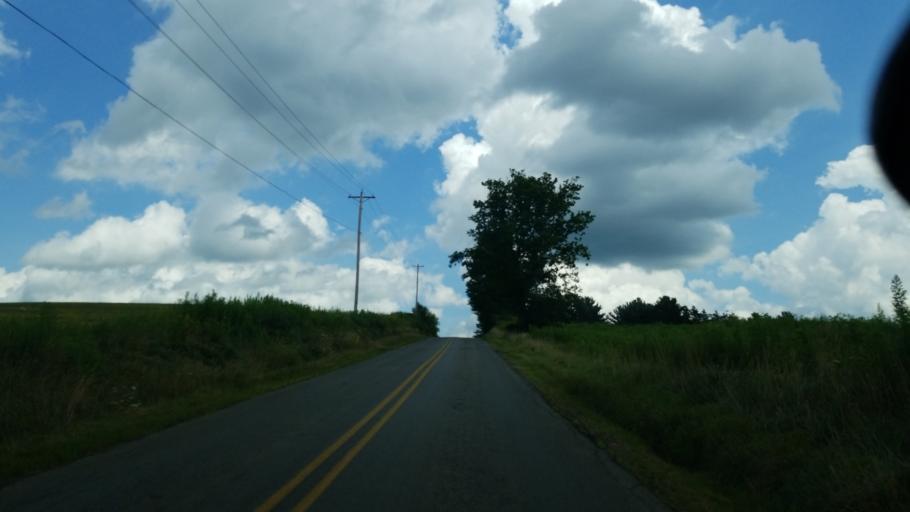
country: US
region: Pennsylvania
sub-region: Jefferson County
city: Brookville
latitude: 41.2282
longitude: -79.0975
